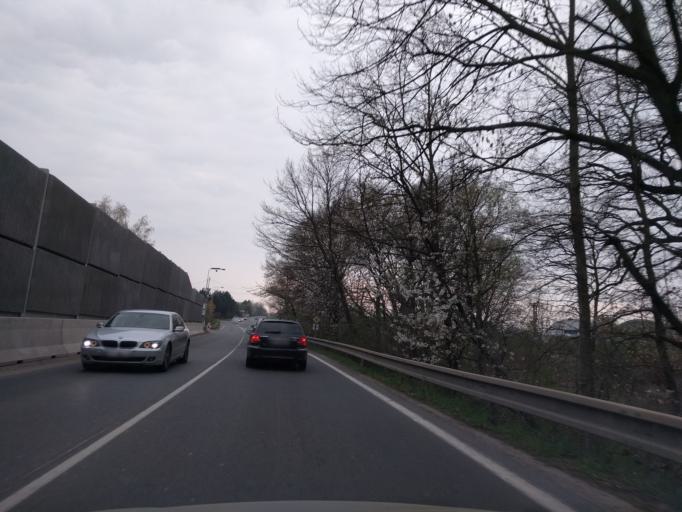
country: CZ
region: Central Bohemia
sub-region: Okres Praha-Vychod
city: Ricany
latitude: 49.9971
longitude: 14.6502
